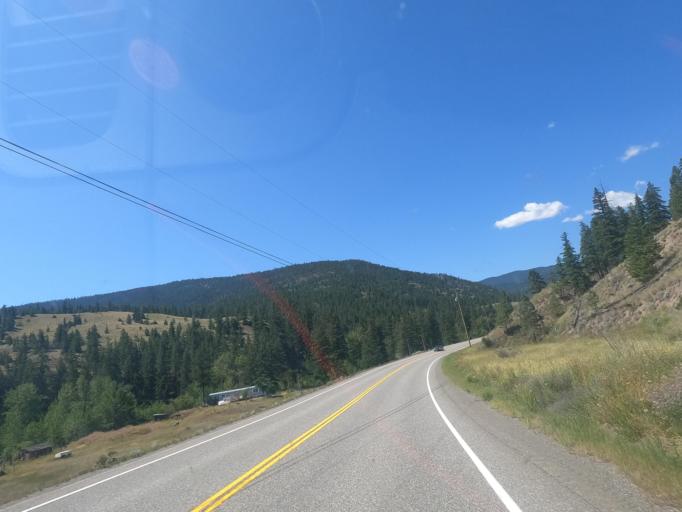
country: CA
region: British Columbia
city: Cache Creek
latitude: 50.8851
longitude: -121.4739
